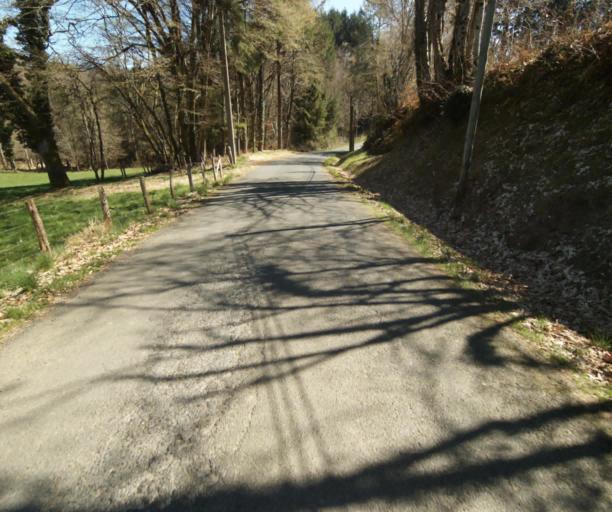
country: FR
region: Limousin
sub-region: Departement de la Correze
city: Saint-Clement
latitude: 45.3404
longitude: 1.7001
